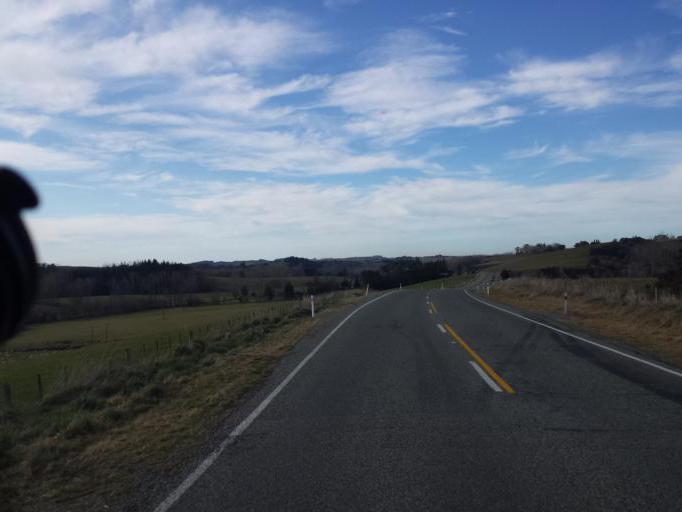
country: NZ
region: Canterbury
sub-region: Timaru District
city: Pleasant Point
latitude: -44.1202
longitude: 171.1168
